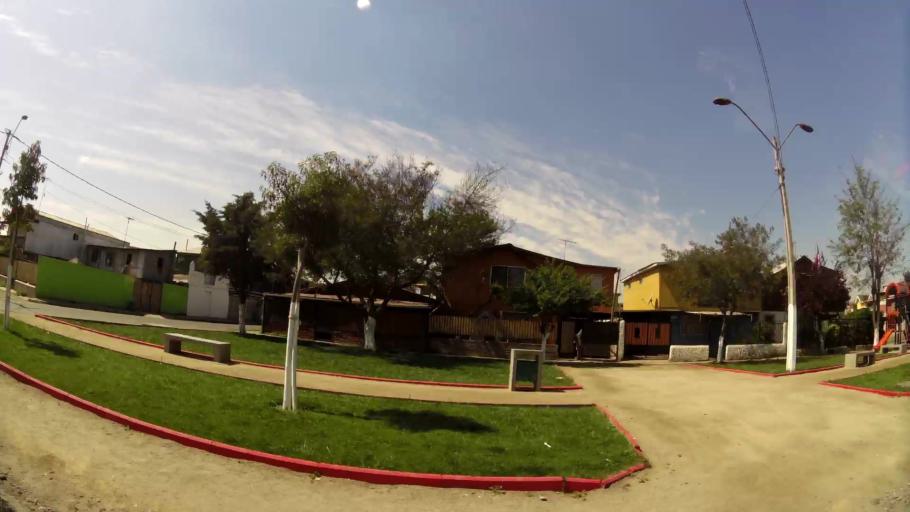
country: CL
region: Santiago Metropolitan
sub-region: Provincia de Santiago
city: La Pintana
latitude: -33.5463
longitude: -70.6367
